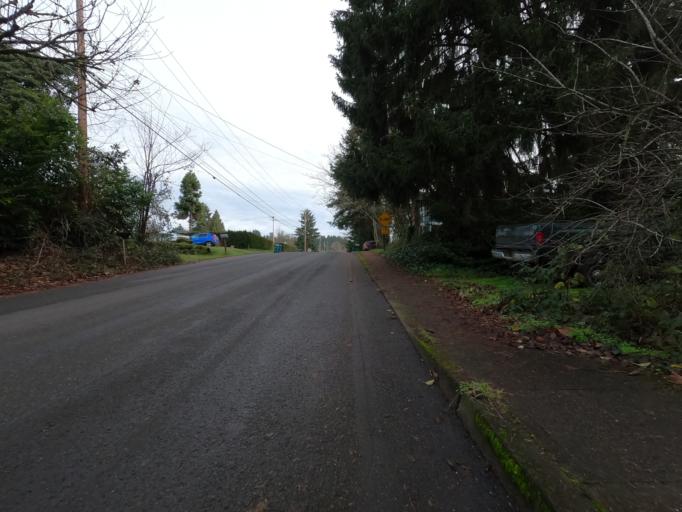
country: US
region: Oregon
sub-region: Clackamas County
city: Jennings Lodge
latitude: 45.3914
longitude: -122.6046
